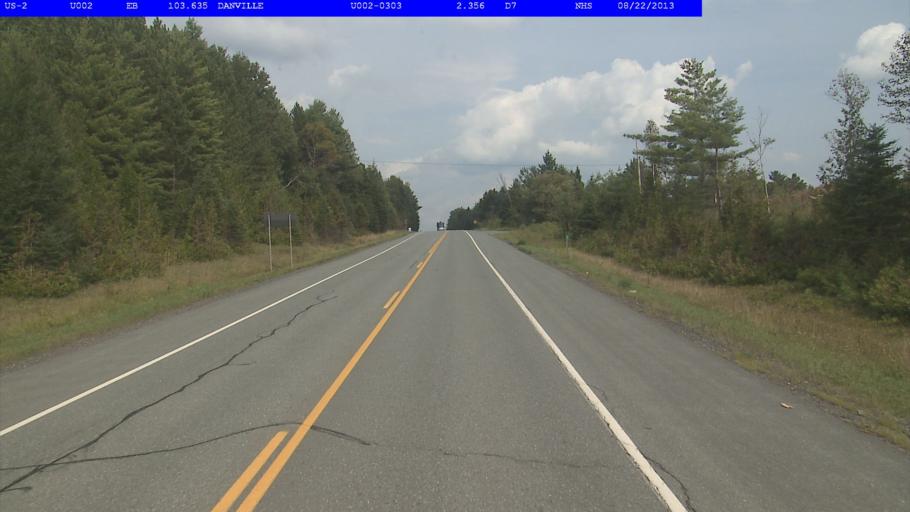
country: US
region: Vermont
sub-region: Caledonia County
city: Saint Johnsbury
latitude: 44.4090
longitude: -72.1817
